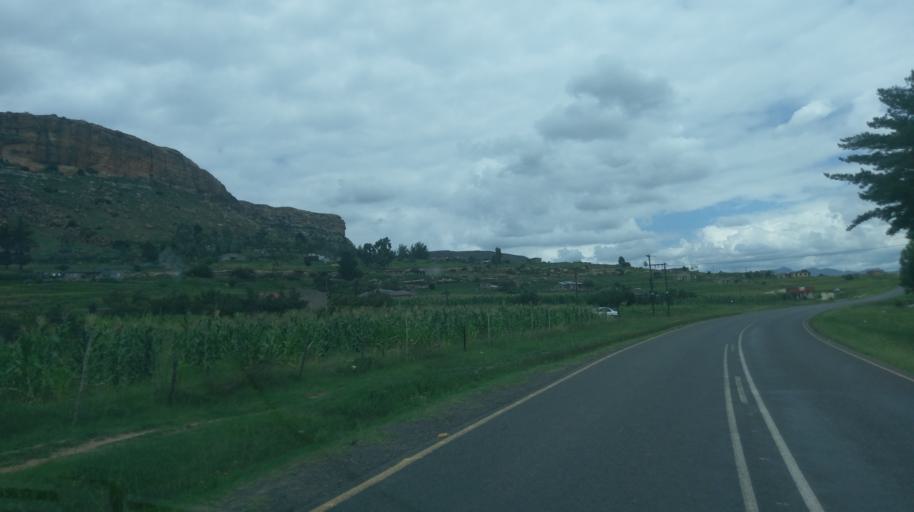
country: LS
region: Leribe
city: Leribe
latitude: -28.9440
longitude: 28.1700
